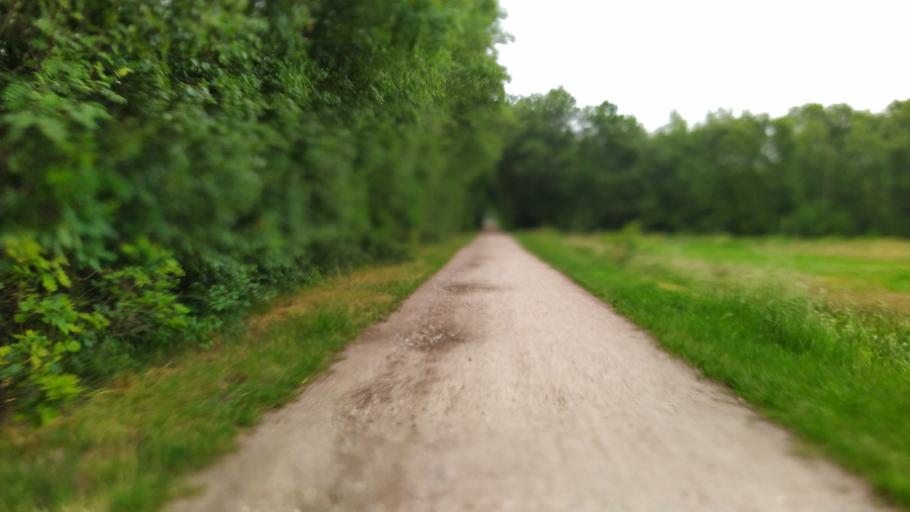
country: DE
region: Lower Saxony
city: Buxtehude
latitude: 53.4777
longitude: 9.6716
